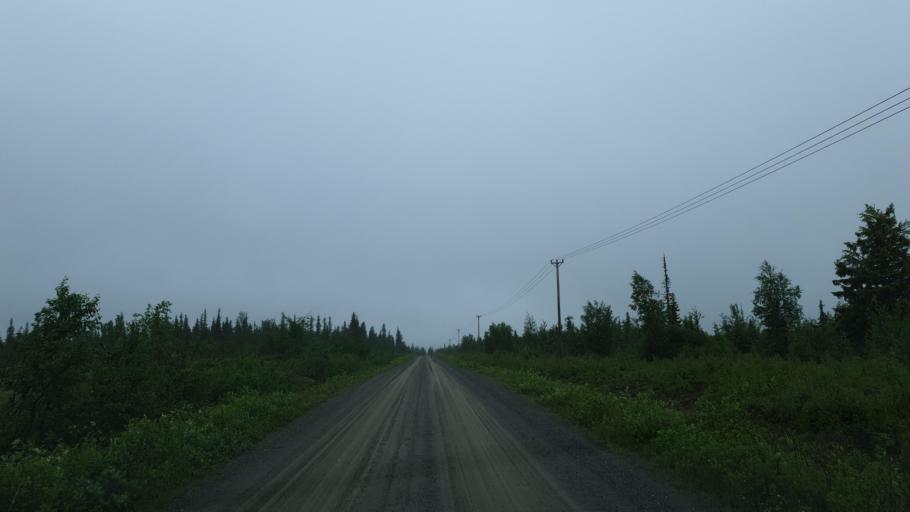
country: SE
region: Vaesterbotten
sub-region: Vilhelmina Kommun
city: Sjoberg
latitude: 65.3140
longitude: 15.9614
